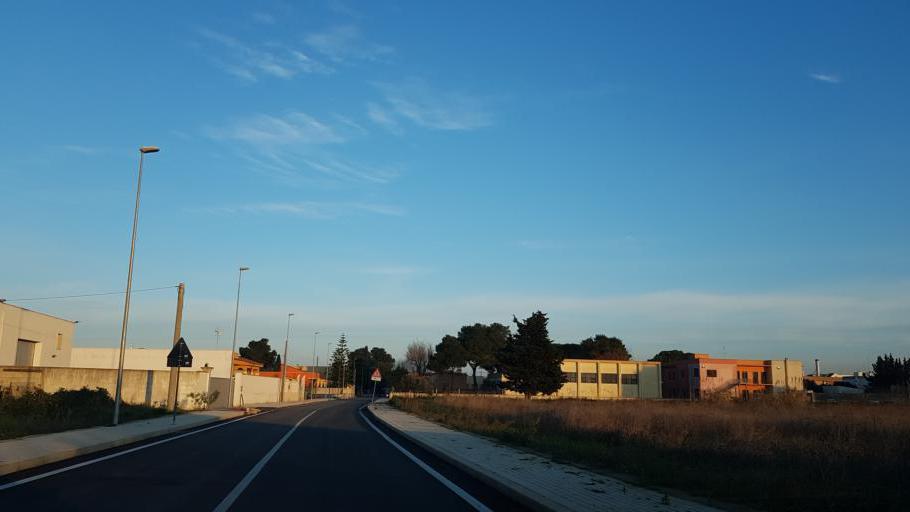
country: IT
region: Apulia
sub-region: Provincia di Brindisi
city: Tuturano
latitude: 40.5463
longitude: 17.9429
